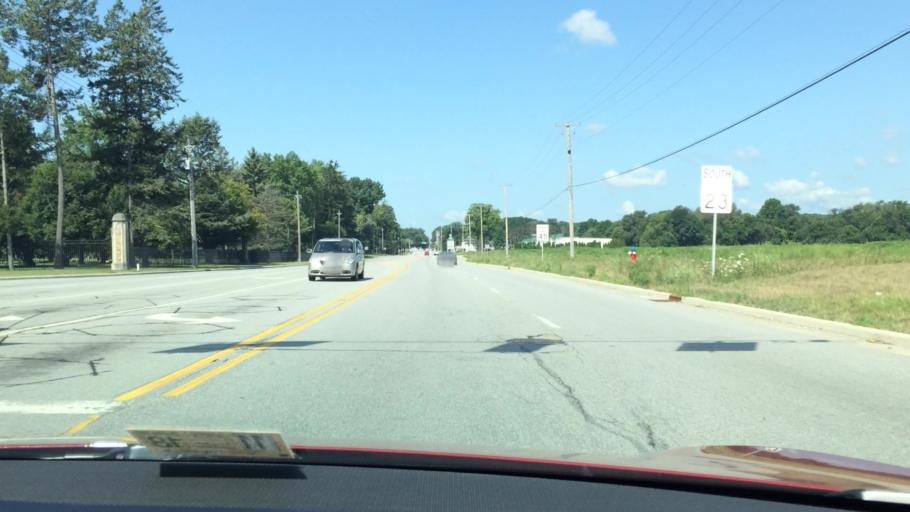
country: US
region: Indiana
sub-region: Saint Joseph County
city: Georgetown
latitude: 41.7241
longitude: -86.1784
